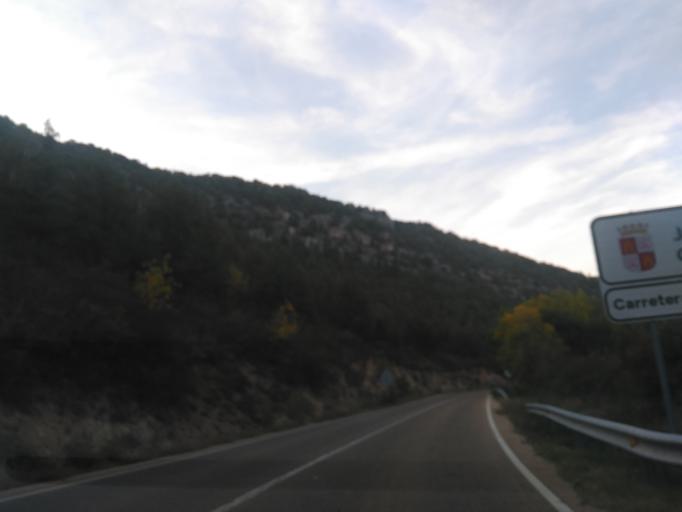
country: ES
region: Castille and Leon
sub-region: Provincia de Soria
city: Ucero
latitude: 41.7252
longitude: -3.0485
